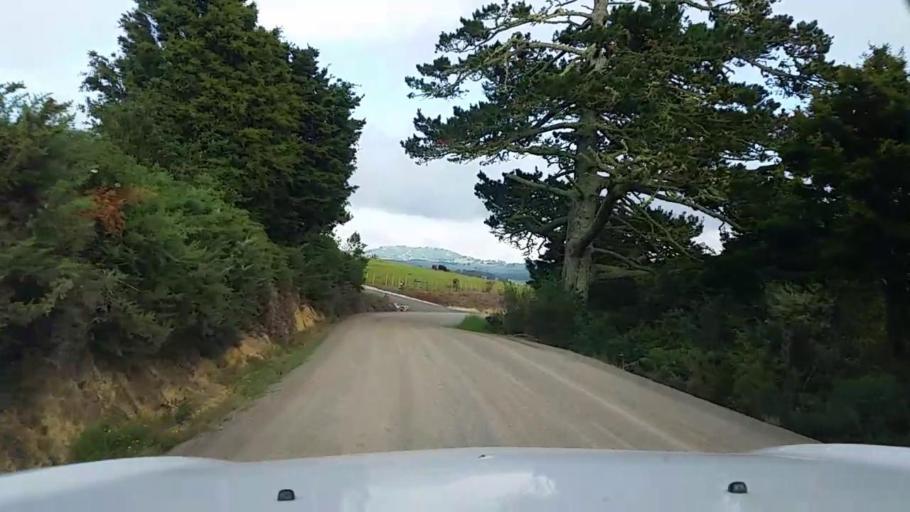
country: NZ
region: Northland
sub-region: Whangarei
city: Maungatapere
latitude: -35.6690
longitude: 174.1754
